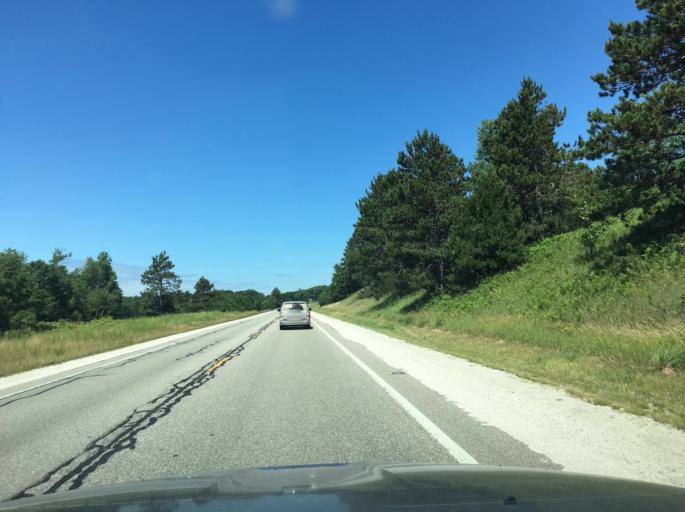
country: US
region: Michigan
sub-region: Osceola County
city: Reed City
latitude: 43.8893
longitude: -85.6459
